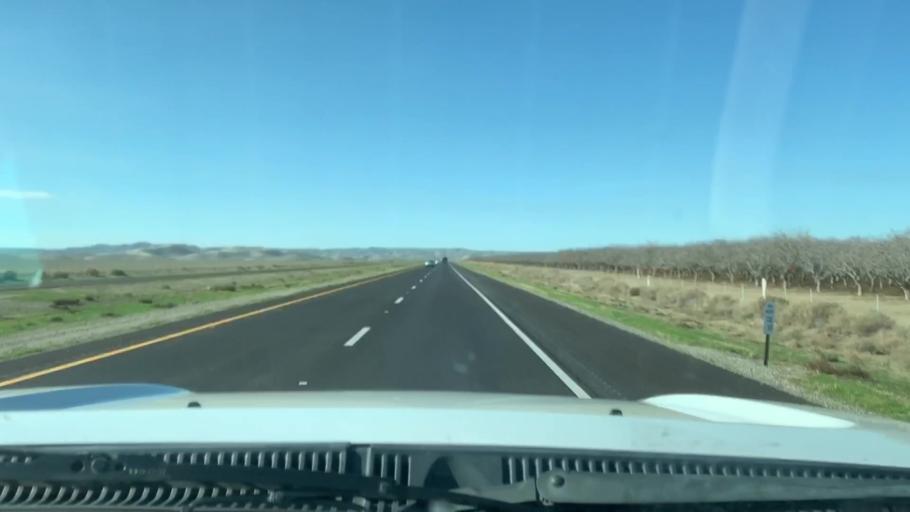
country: US
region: California
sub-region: Kern County
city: Lost Hills
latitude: 35.6147
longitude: -119.9299
